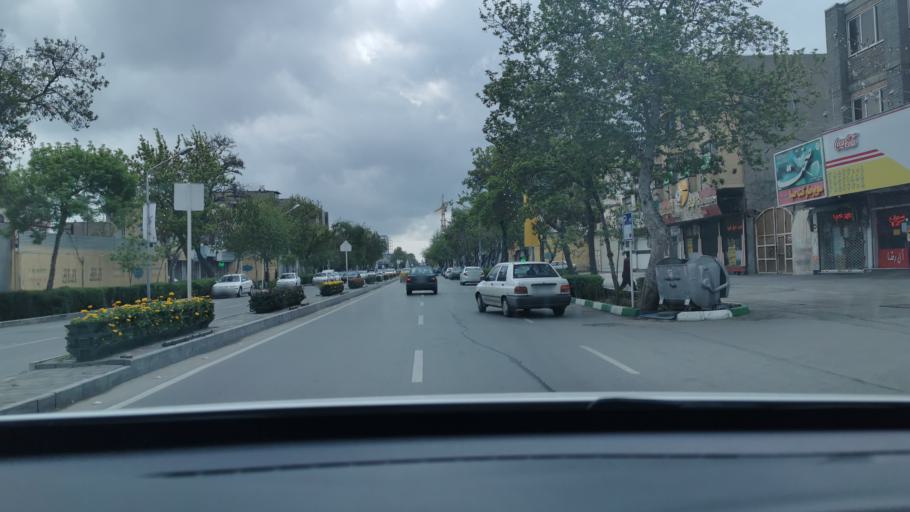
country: IR
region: Razavi Khorasan
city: Mashhad
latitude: 36.2761
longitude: 59.6009
